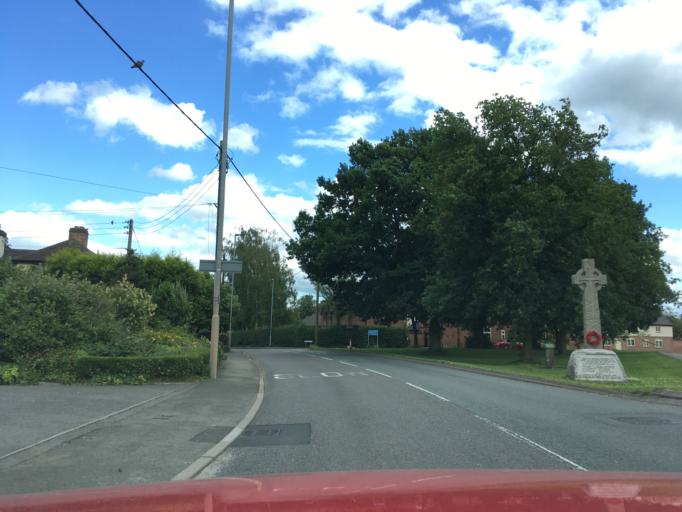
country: GB
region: England
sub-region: Leicestershire
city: Measham
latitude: 52.6413
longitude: -1.5037
